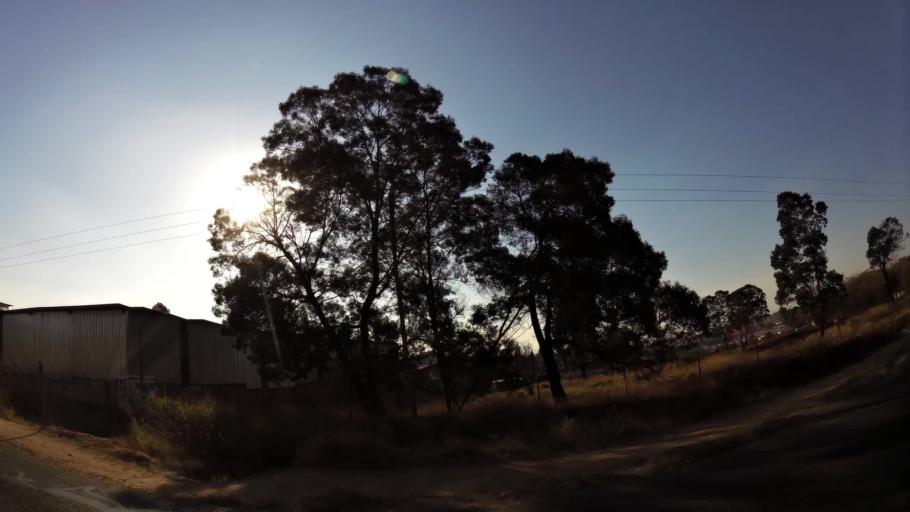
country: ZA
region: Gauteng
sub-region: West Rand District Municipality
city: Muldersdriseloop
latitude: -26.0237
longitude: 27.8731
